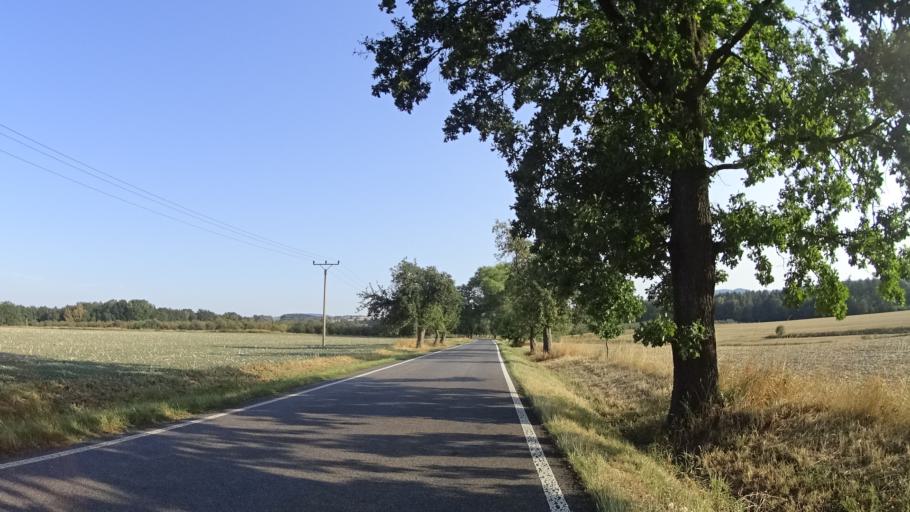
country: CZ
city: Ohrazenice
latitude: 50.6068
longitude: 15.1282
